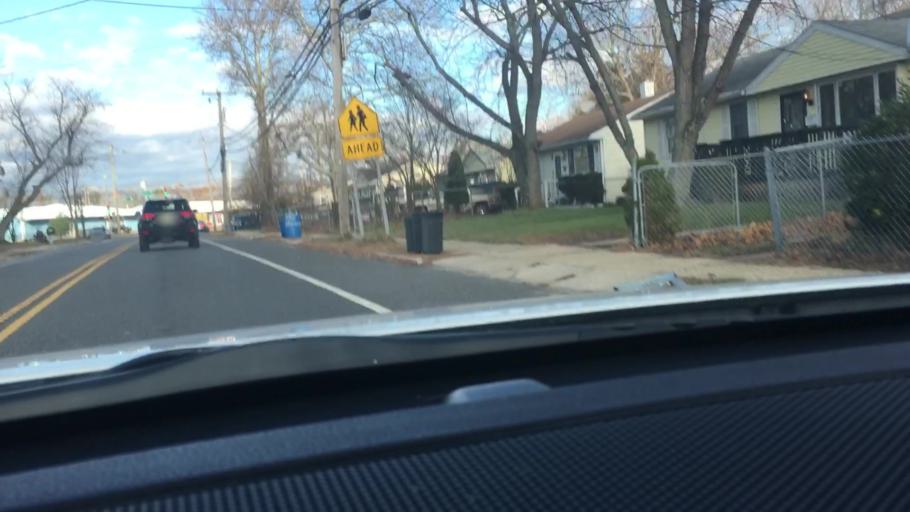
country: US
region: New Jersey
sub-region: Atlantic County
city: Pleasantville
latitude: 39.4108
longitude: -74.5182
